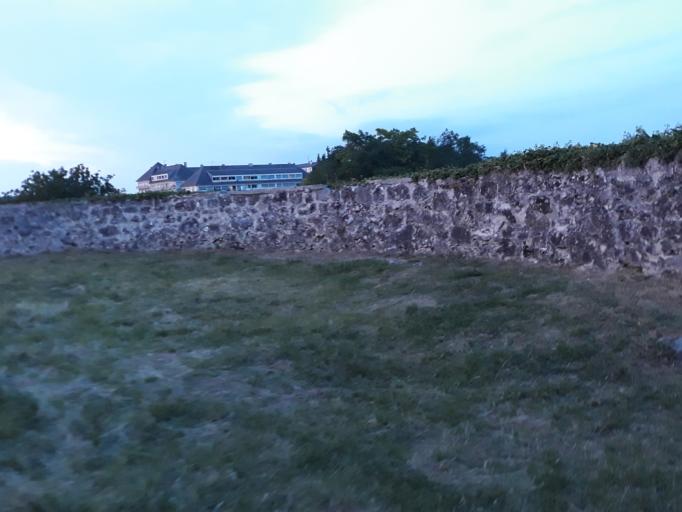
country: FR
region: Picardie
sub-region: Departement de l'Aisne
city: Laon
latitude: 49.5532
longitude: 3.6136
